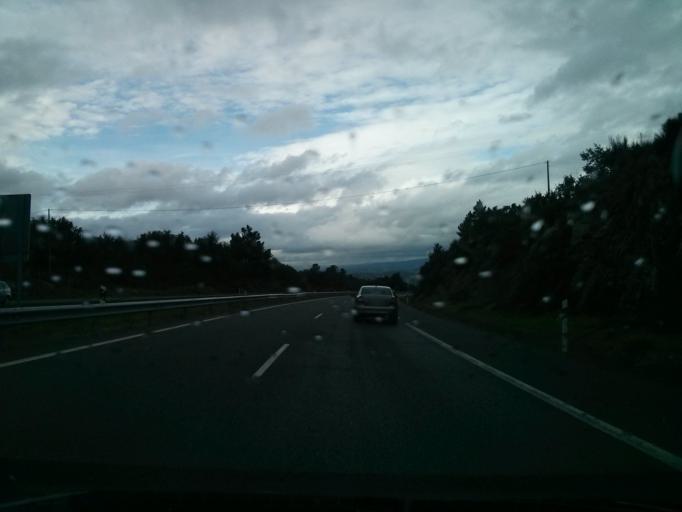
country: ES
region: Galicia
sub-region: Provincia de Ourense
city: Taboadela
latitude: 42.2683
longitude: -7.8707
